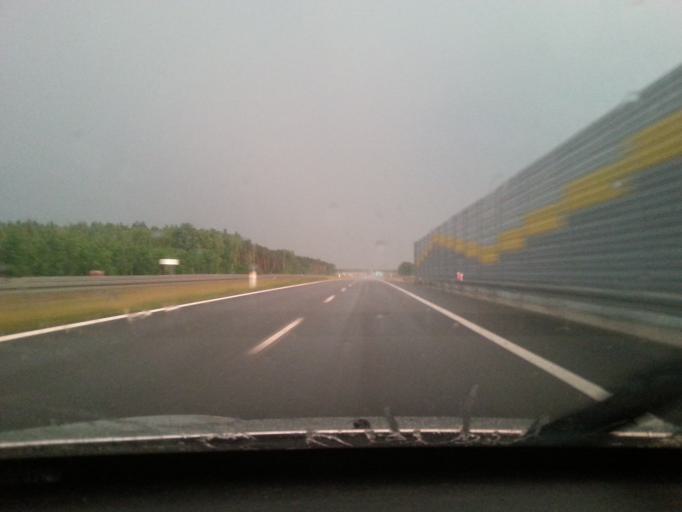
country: PL
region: Lodz Voivodeship
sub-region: Powiat pabianicki
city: Dobron
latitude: 51.6152
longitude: 19.2749
